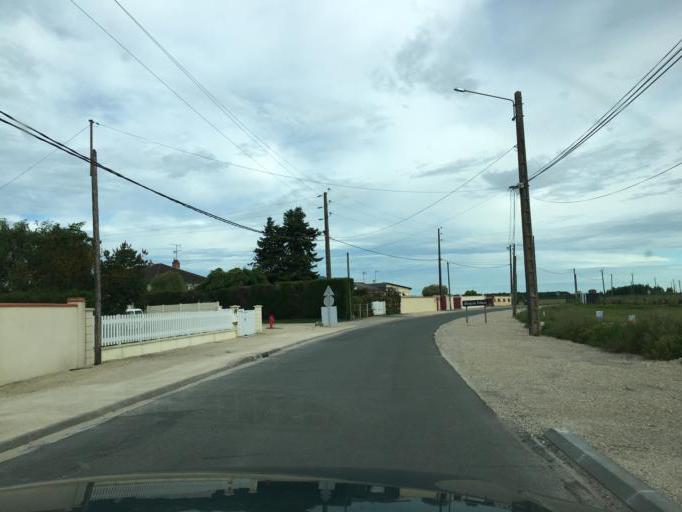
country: FR
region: Centre
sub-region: Departement du Loiret
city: Chaingy
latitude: 47.9370
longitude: 1.7630
